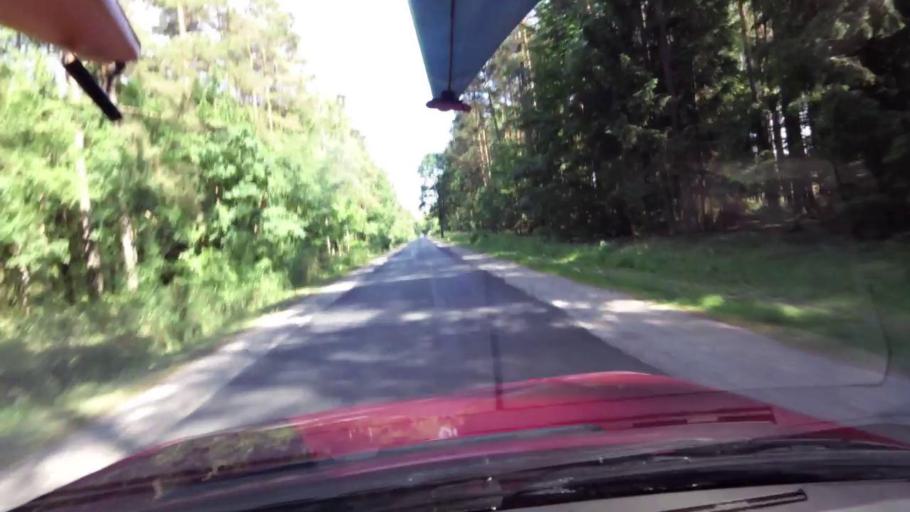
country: PL
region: Pomeranian Voivodeship
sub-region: Powiat bytowski
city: Miastko
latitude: 54.1110
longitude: 16.9604
